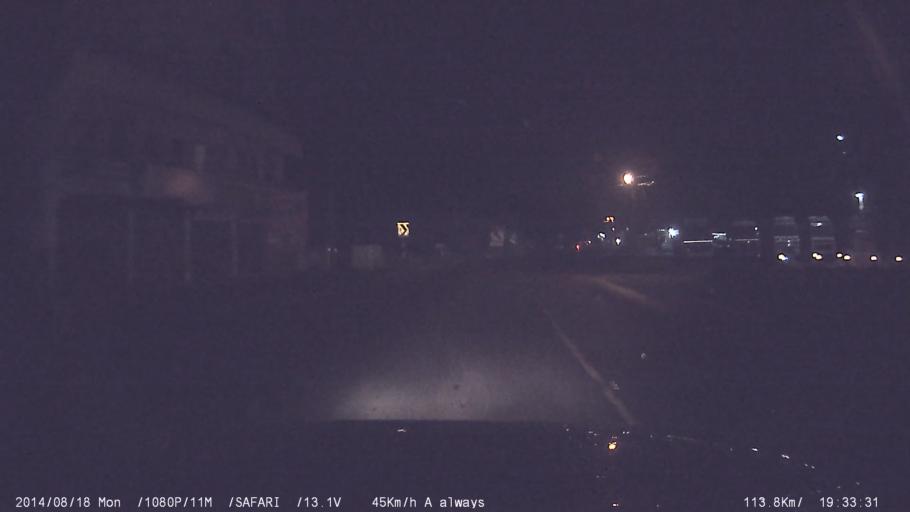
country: IN
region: Kerala
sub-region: Ernakulam
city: Perumbavoor
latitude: 10.1046
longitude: 76.4830
